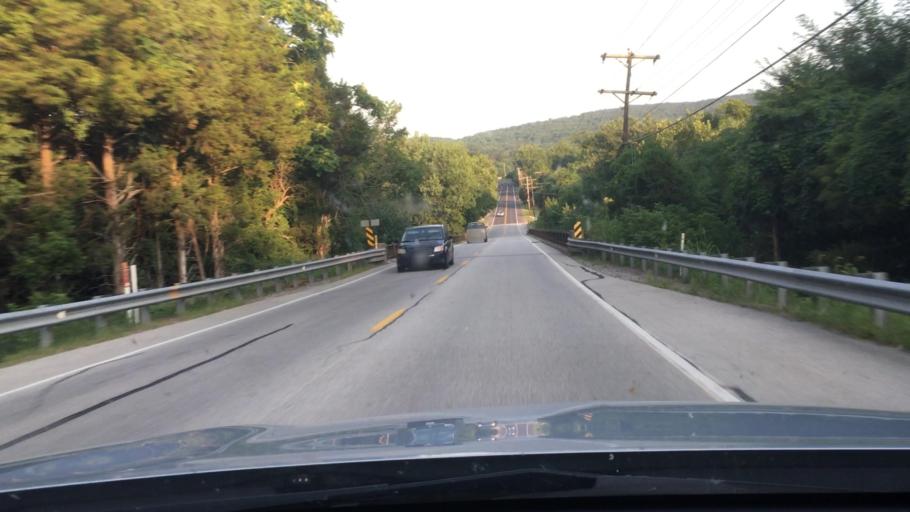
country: US
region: Pennsylvania
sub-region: York County
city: Dover
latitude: 40.0456
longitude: -76.8995
